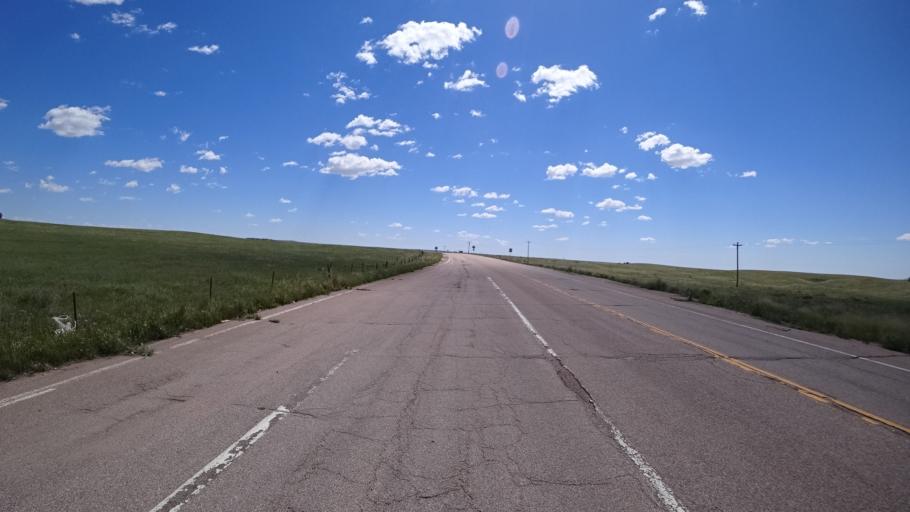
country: US
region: Colorado
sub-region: El Paso County
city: Cimarron Hills
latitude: 38.8379
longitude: -104.6819
